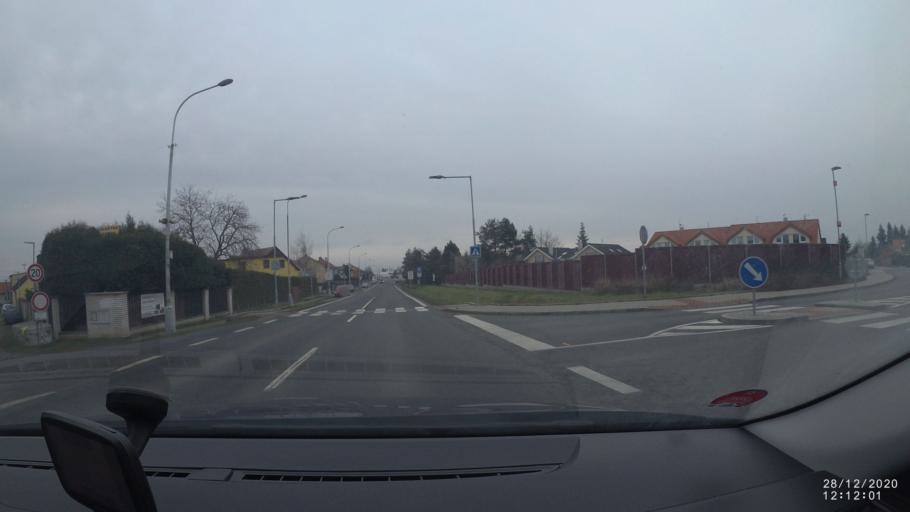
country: CZ
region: Central Bohemia
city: Brandys nad Labem-Stara Boleslav
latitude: 50.1755
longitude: 14.6507
